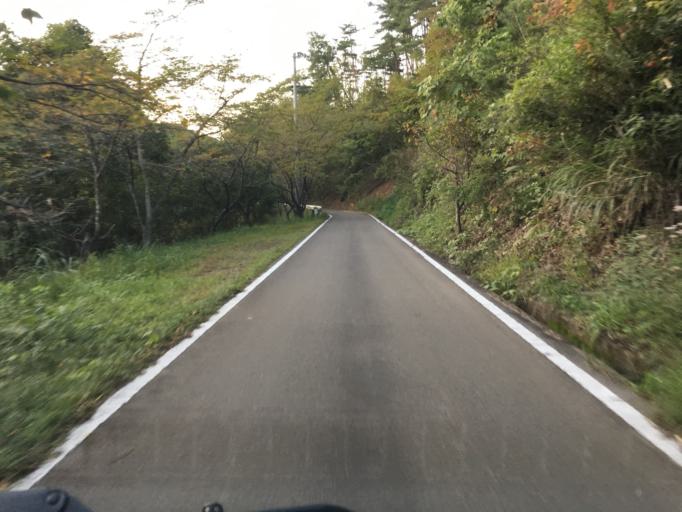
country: JP
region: Fukushima
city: Yanagawamachi-saiwaicho
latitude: 37.8484
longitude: 140.6327
